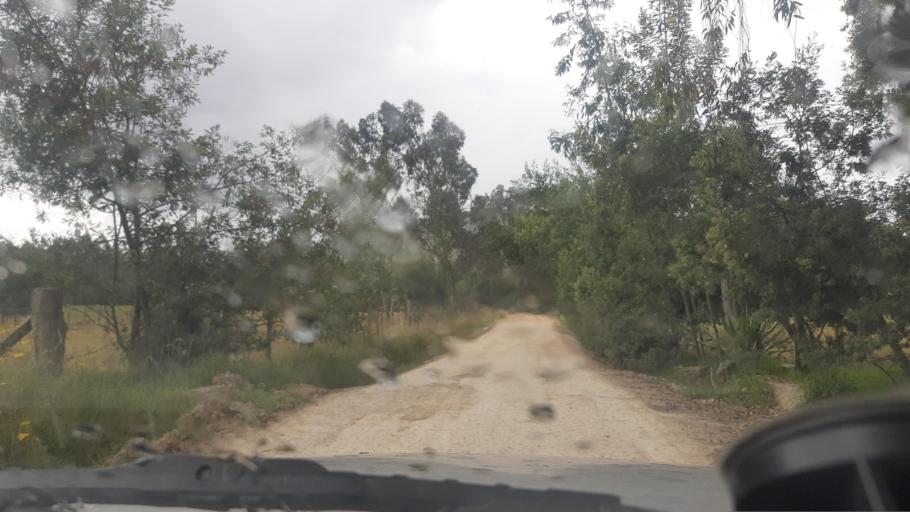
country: CO
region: Cundinamarca
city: Cucunuba
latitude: 5.1916
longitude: -73.7936
